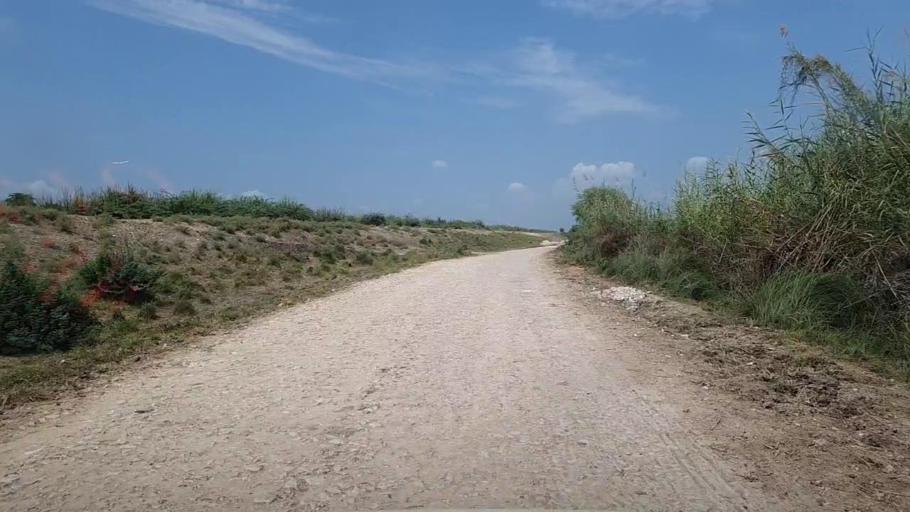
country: PK
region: Sindh
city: Bhiria
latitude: 26.9073
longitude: 68.2018
